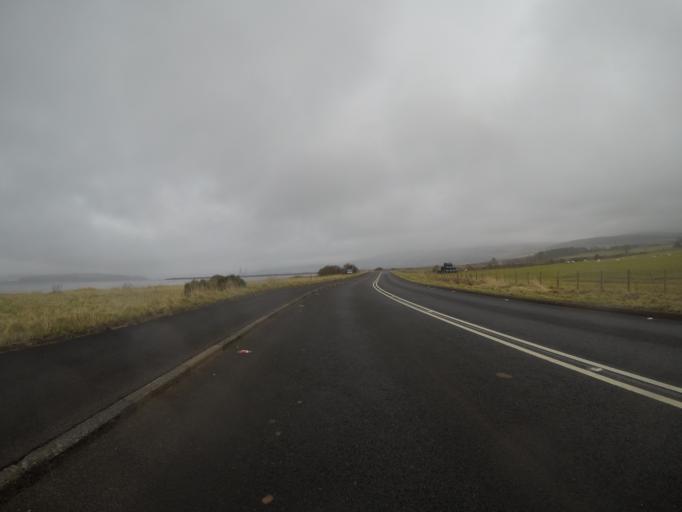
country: GB
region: Scotland
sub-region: North Ayrshire
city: Millport
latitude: 55.7253
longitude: -4.8975
